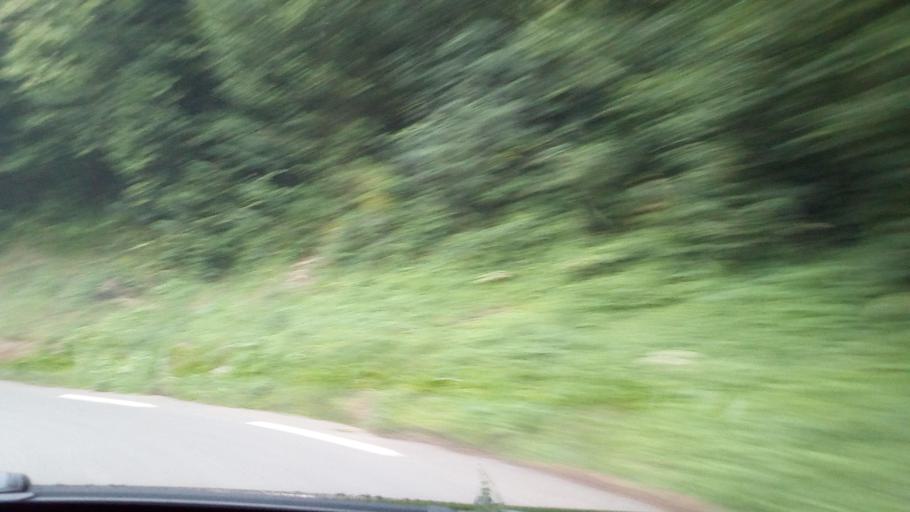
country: FR
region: Midi-Pyrenees
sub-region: Departement des Hautes-Pyrenees
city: Cauterets
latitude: 42.9623
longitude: -0.2191
